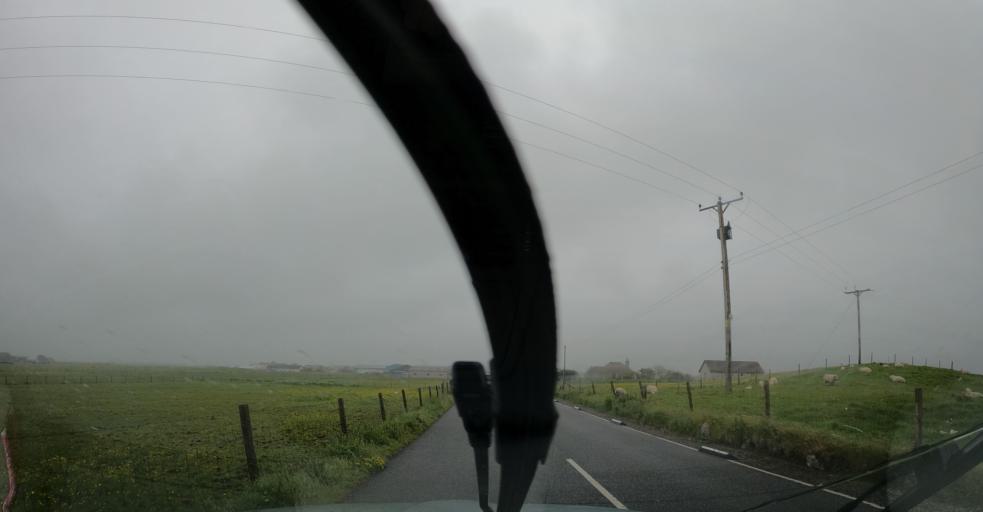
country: GB
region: Scotland
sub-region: Eilean Siar
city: Benbecula
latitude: 57.4721
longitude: -7.3702
